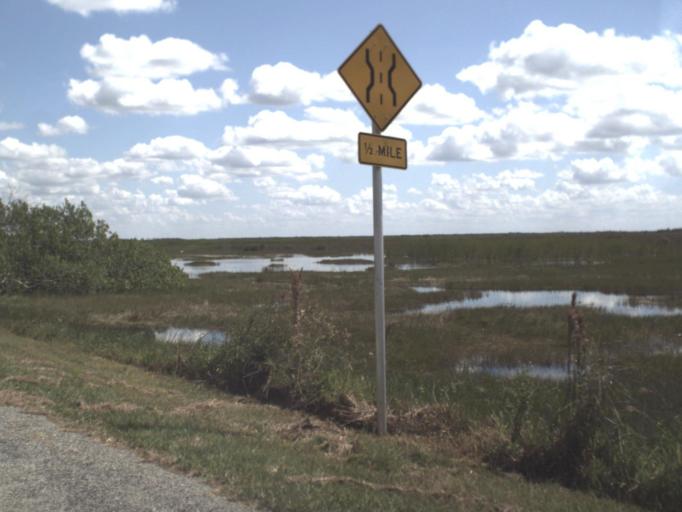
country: US
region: Florida
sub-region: Collier County
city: Marco
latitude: 25.9239
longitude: -81.4186
